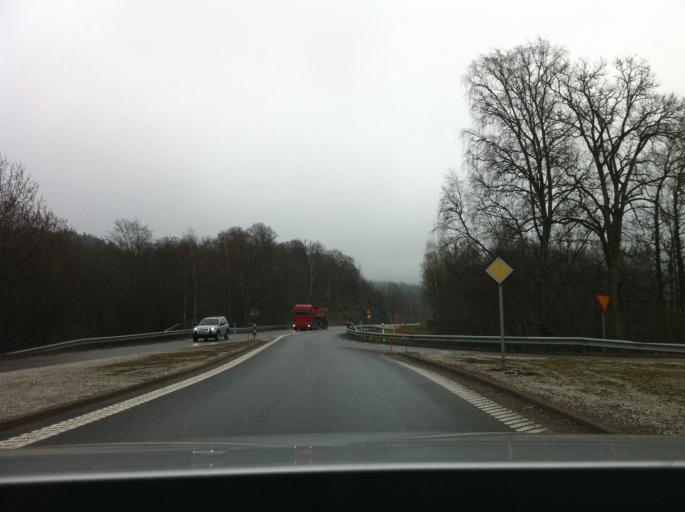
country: SE
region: Vaestra Goetaland
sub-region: Alingsas Kommun
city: Alingsas
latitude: 57.9756
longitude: 12.4333
